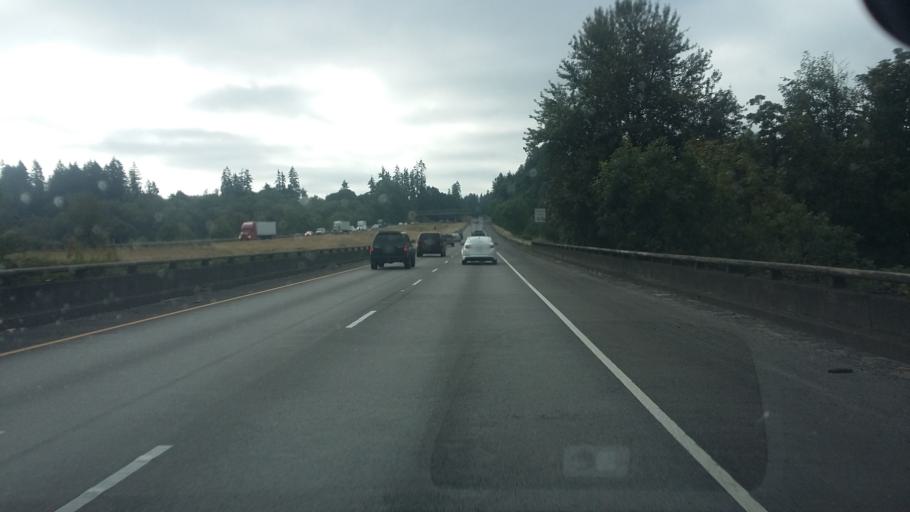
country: US
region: Washington
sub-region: Clark County
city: Salmon Creek
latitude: 45.7111
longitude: -122.6388
